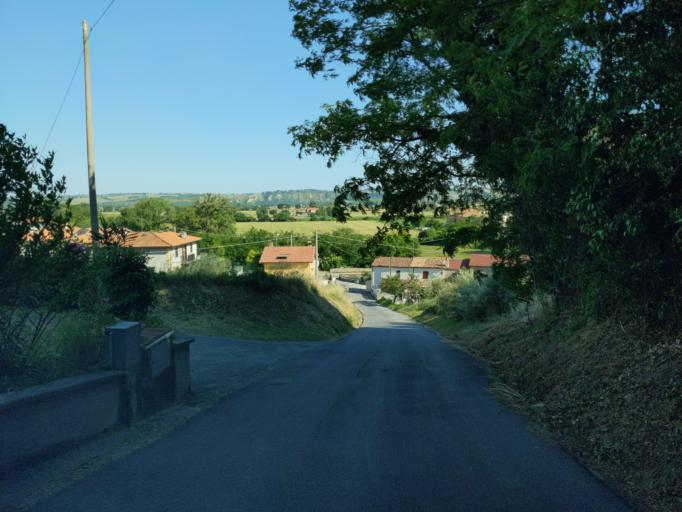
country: IT
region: The Marches
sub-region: Provincia di Pesaro e Urbino
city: Cuccurano
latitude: 43.7979
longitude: 12.9601
